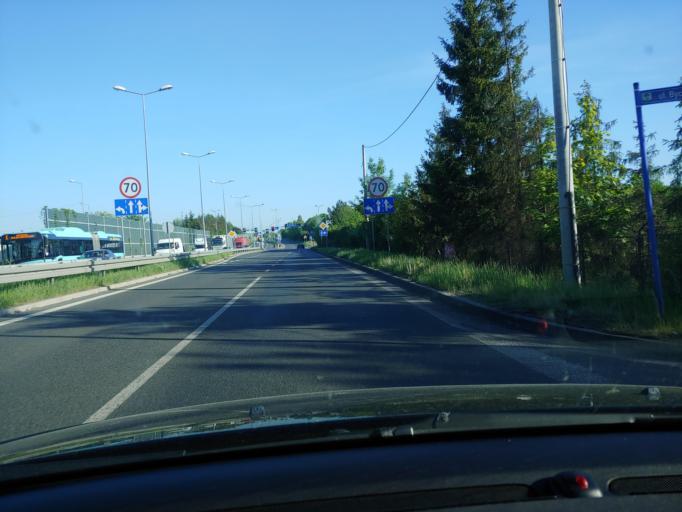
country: PL
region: Silesian Voivodeship
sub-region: Jaworzno
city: Jaworzno
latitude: 50.1819
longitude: 19.2903
